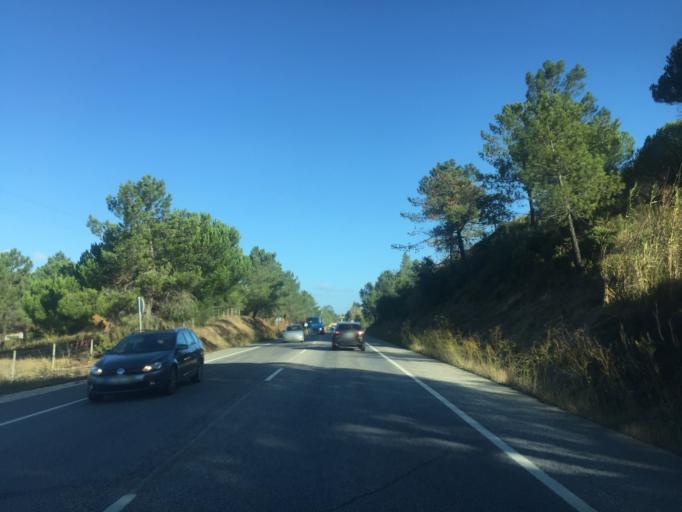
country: PT
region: Lisbon
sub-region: Azambuja
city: Alcoentre
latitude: 39.2178
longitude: -8.9537
